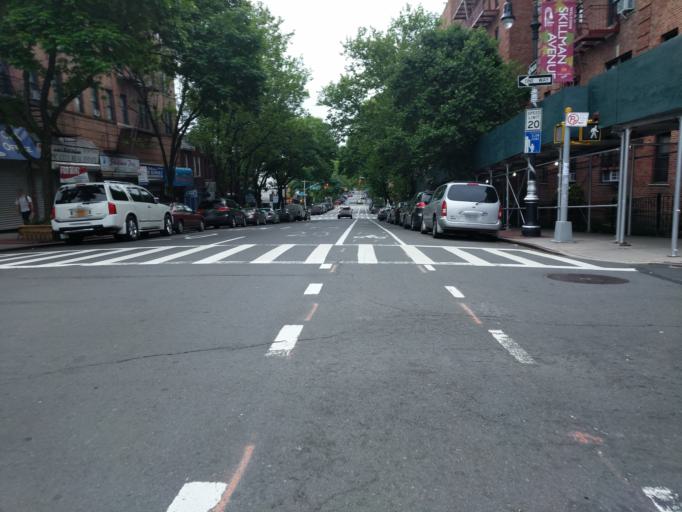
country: US
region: New York
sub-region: Queens County
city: Long Island City
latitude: 40.7462
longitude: -73.9143
